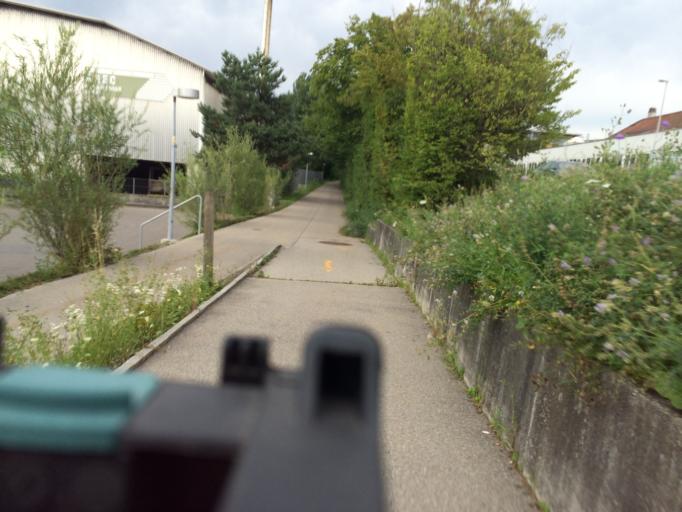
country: CH
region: Bern
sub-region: Bern-Mittelland District
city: Zollikofen
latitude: 46.9809
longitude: 7.4568
